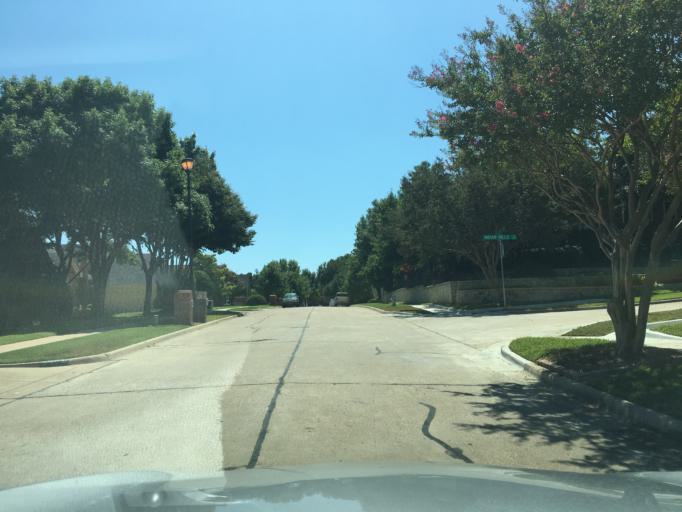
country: US
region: Texas
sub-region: Dallas County
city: Sachse
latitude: 32.9690
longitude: -96.6292
